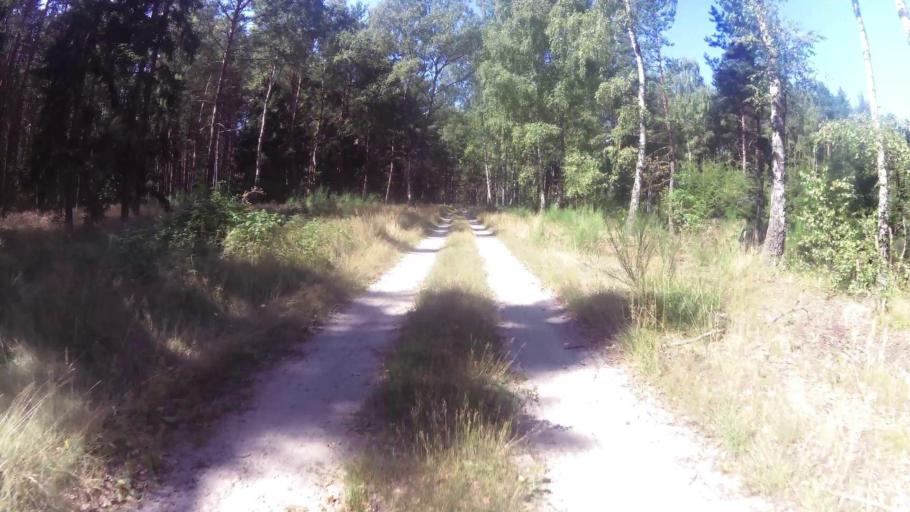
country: PL
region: West Pomeranian Voivodeship
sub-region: Powiat stargardzki
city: Insko
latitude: 53.4388
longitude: 15.5997
